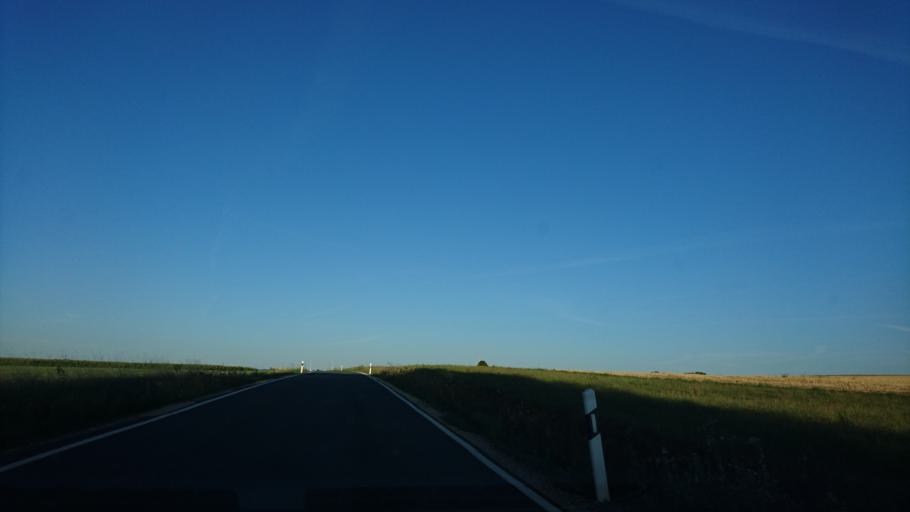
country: DE
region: Bavaria
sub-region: Regierungsbezirk Mittelfranken
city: Nennslingen
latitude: 49.0509
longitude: 11.1570
